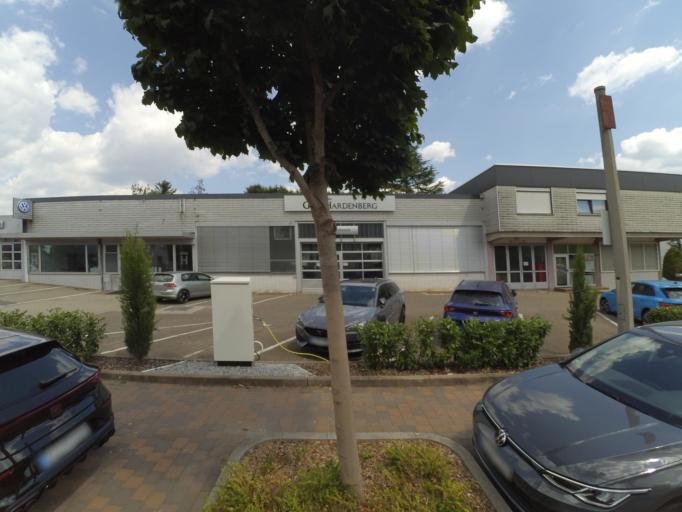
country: DE
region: Baden-Wuerttemberg
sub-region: Karlsruhe Region
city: Eggenstein-Leopoldshafen
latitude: 49.0731
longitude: 8.3920
